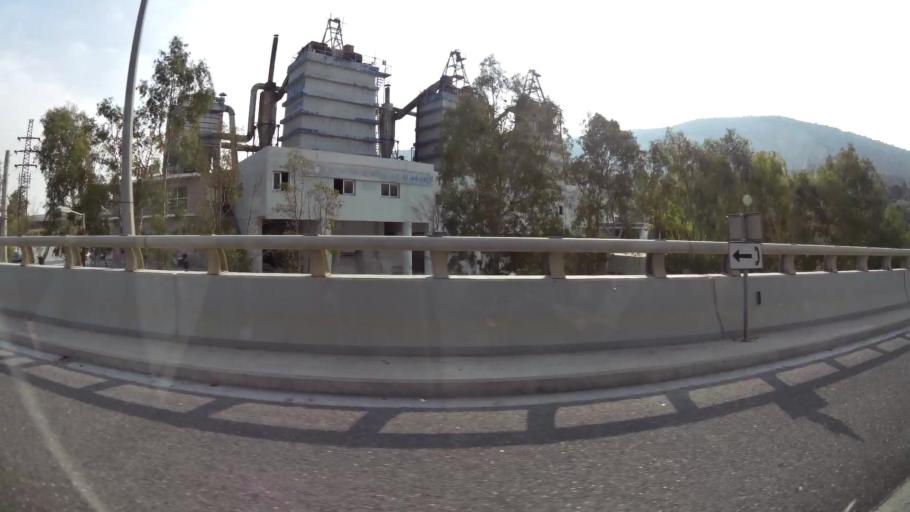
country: GR
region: Attica
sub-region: Nomarchia Athinas
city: Petroupolis
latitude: 38.0639
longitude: 23.6679
